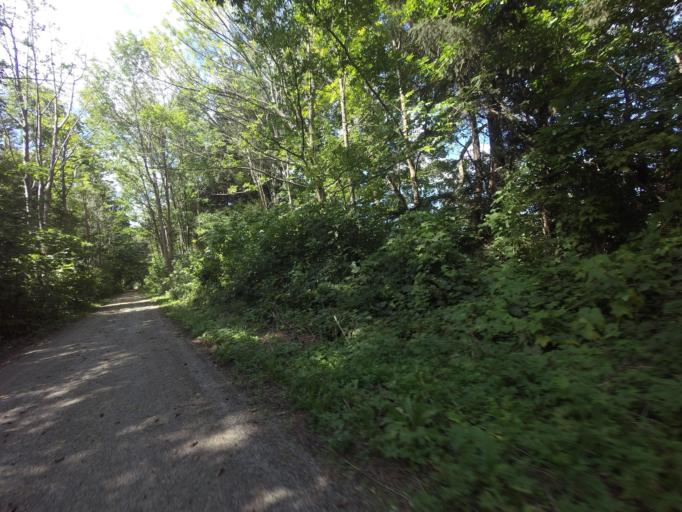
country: CA
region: Ontario
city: Huron East
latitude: 43.6776
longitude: -81.2933
